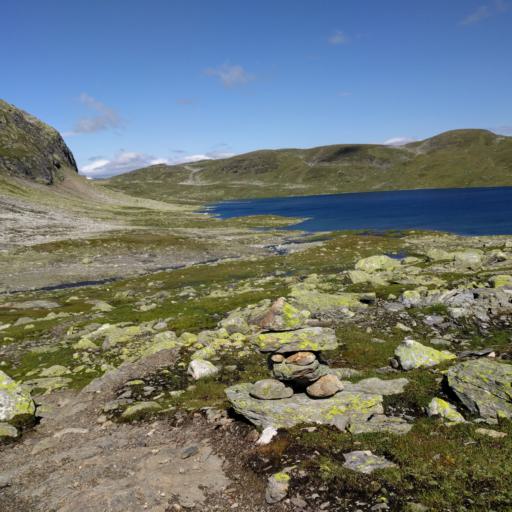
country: NO
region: Aust-Agder
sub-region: Bykle
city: Hovden
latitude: 59.8672
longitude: 7.2160
